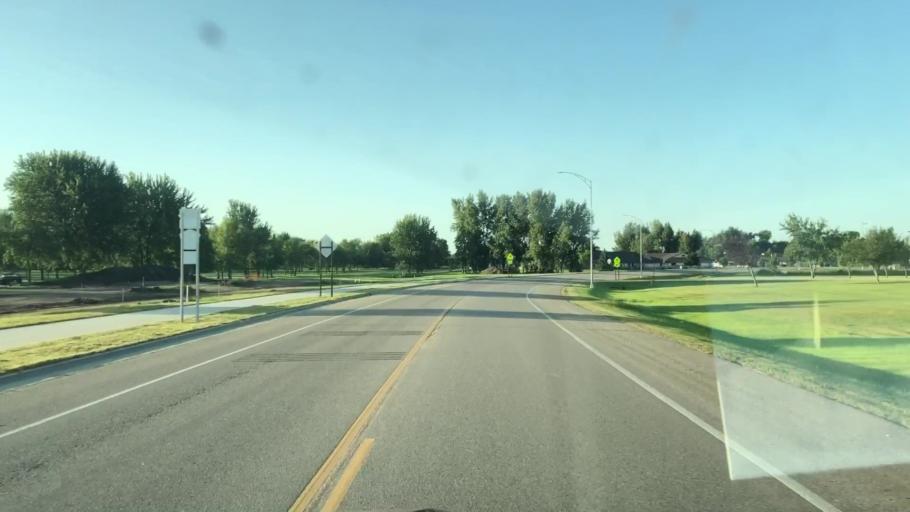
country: US
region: Minnesota
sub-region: Nobles County
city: Worthington
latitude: 43.6293
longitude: -95.6286
